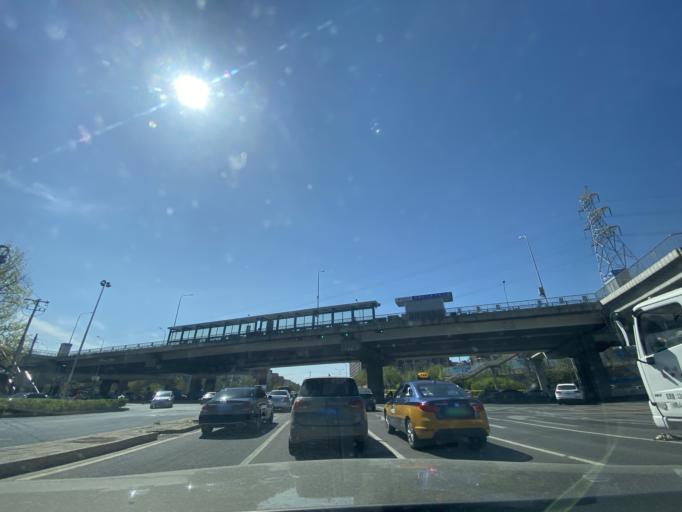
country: CN
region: Beijing
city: Babaoshan
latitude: 39.9251
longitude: 116.2468
